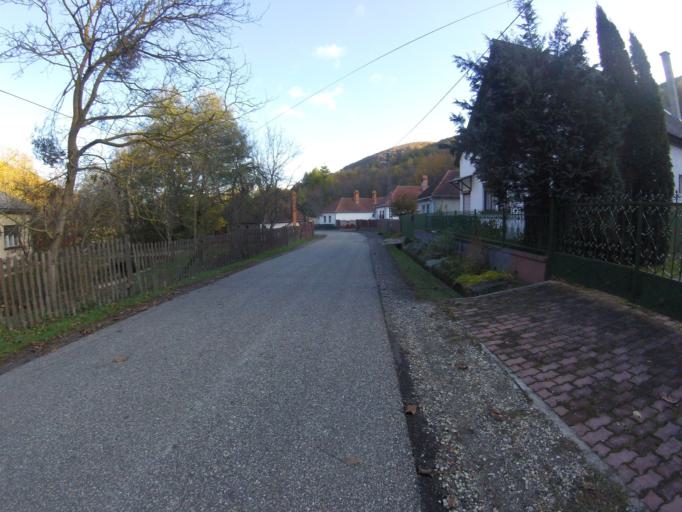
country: HU
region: Borsod-Abauj-Zemplen
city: Tolcsva
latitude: 48.3790
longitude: 21.3946
